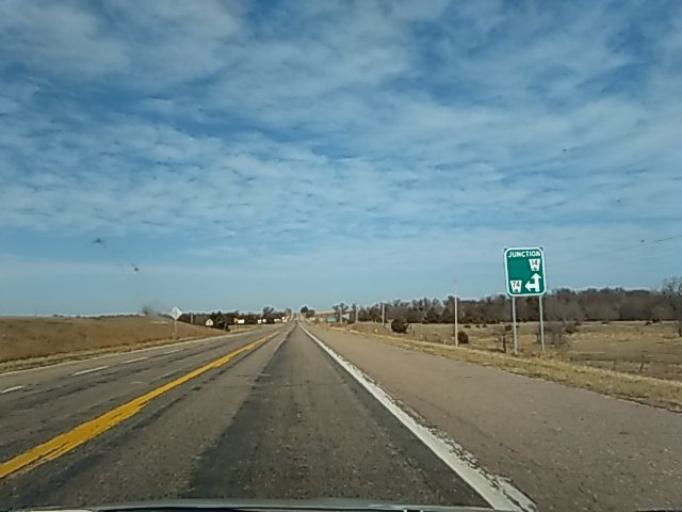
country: US
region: Nebraska
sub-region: Clay County
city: Clay Center
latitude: 40.4346
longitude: -98.0514
